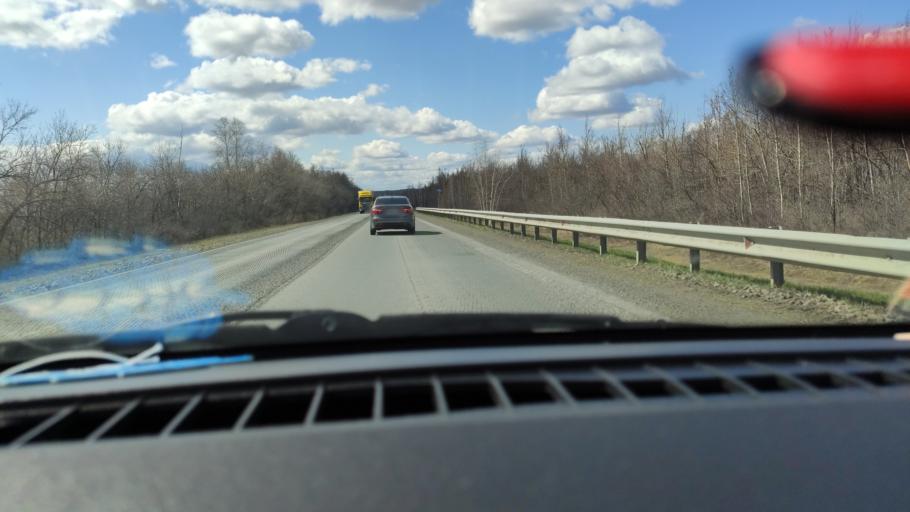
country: RU
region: Saratov
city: Dukhovnitskoye
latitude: 52.6682
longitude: 48.2188
